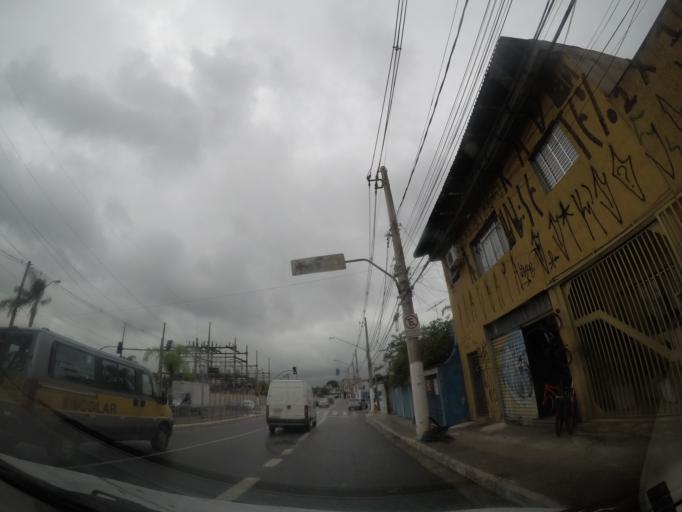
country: BR
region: Sao Paulo
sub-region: Guarulhos
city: Guarulhos
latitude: -23.4855
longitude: -46.4812
